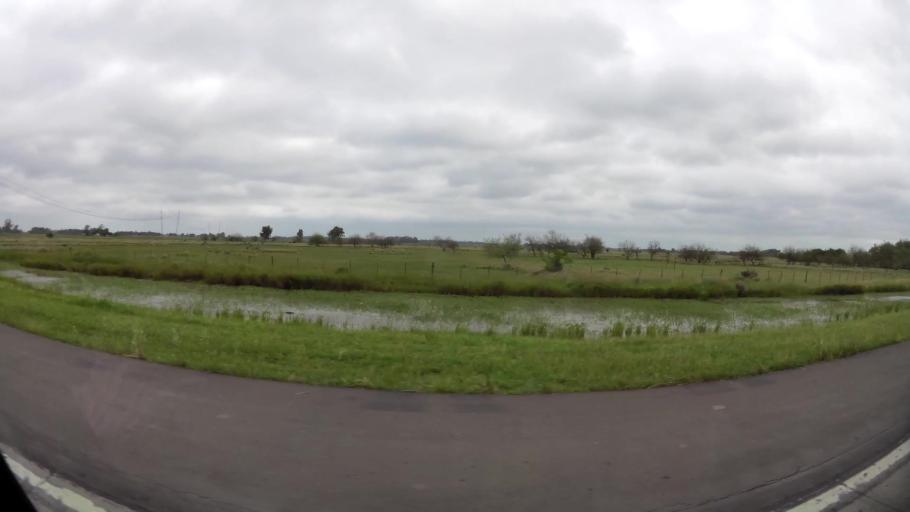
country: AR
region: Buenos Aires
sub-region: Partido de Brandsen
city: Brandsen
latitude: -35.0474
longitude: -58.1396
